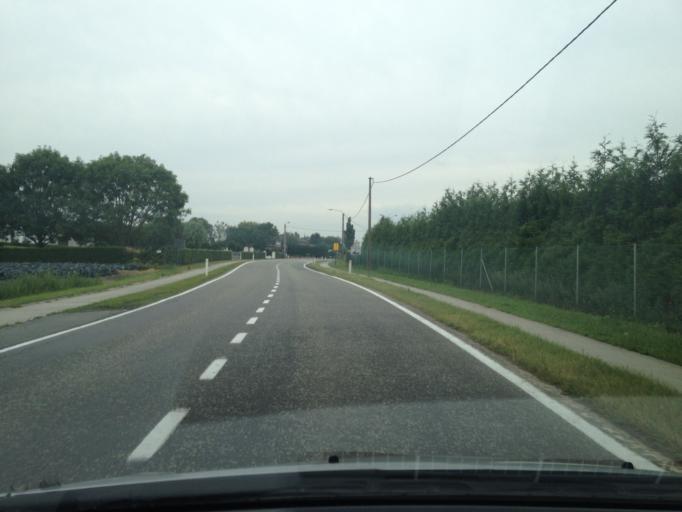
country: BE
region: Flanders
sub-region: Provincie West-Vlaanderen
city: Gistel
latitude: 51.1338
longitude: 2.9079
